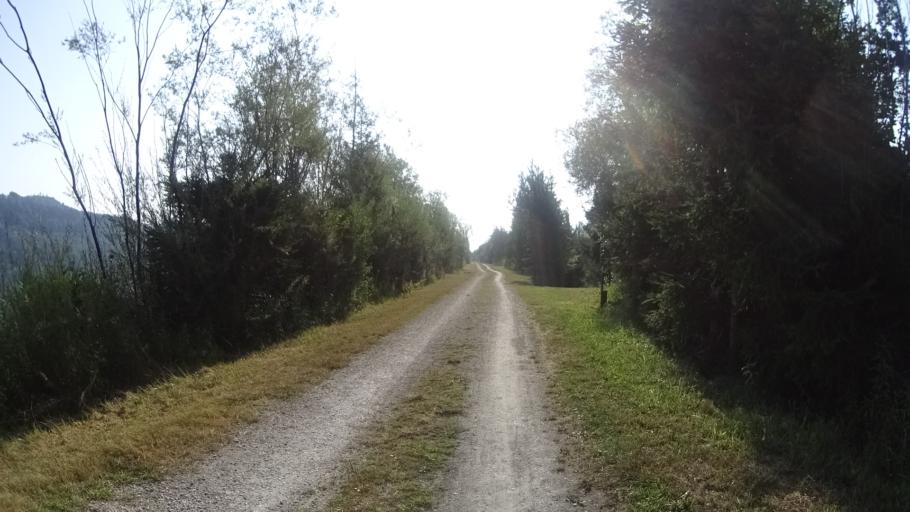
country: AT
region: Carinthia
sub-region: Politischer Bezirk Klagenfurt Land
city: Kottmannsdorf
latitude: 46.5430
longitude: 14.2353
